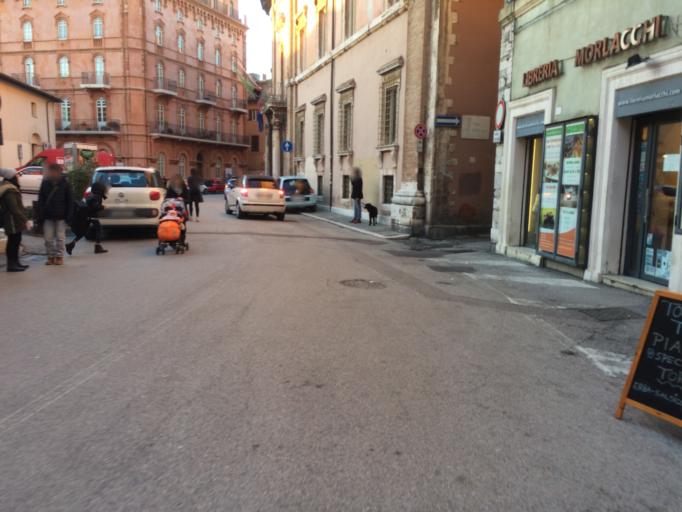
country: IT
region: Umbria
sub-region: Provincia di Perugia
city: Perugia
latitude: 43.1130
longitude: 12.3876
